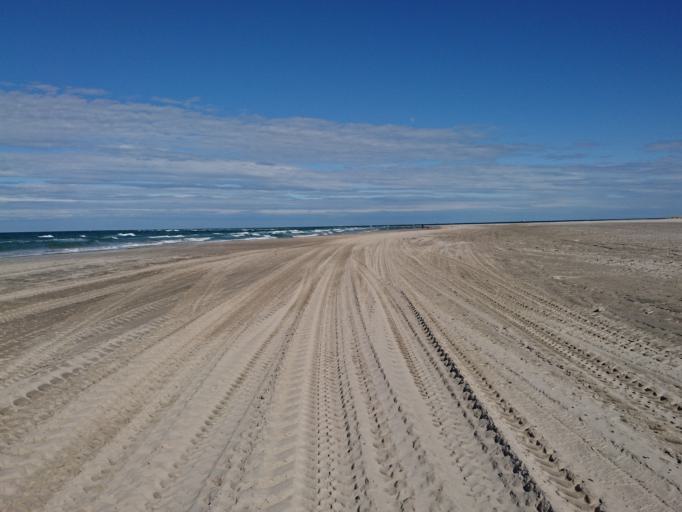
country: DK
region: North Denmark
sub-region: Frederikshavn Kommune
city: Skagen
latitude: 57.7480
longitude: 10.6433
